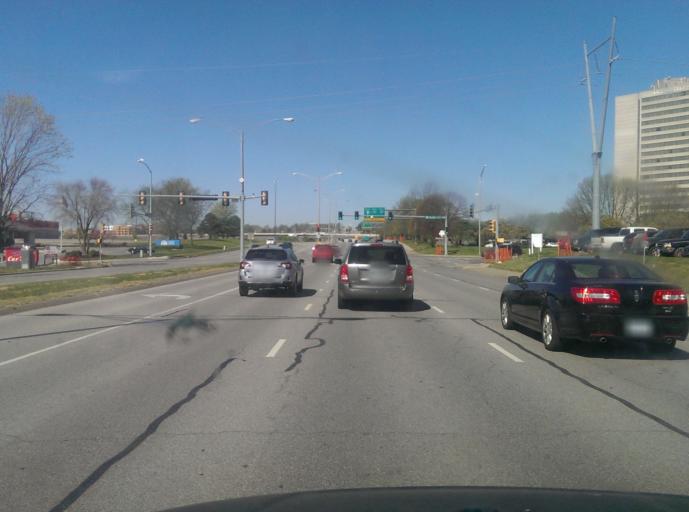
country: US
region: Kansas
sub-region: Johnson County
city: Lenexa
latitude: 38.9276
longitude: -94.6995
